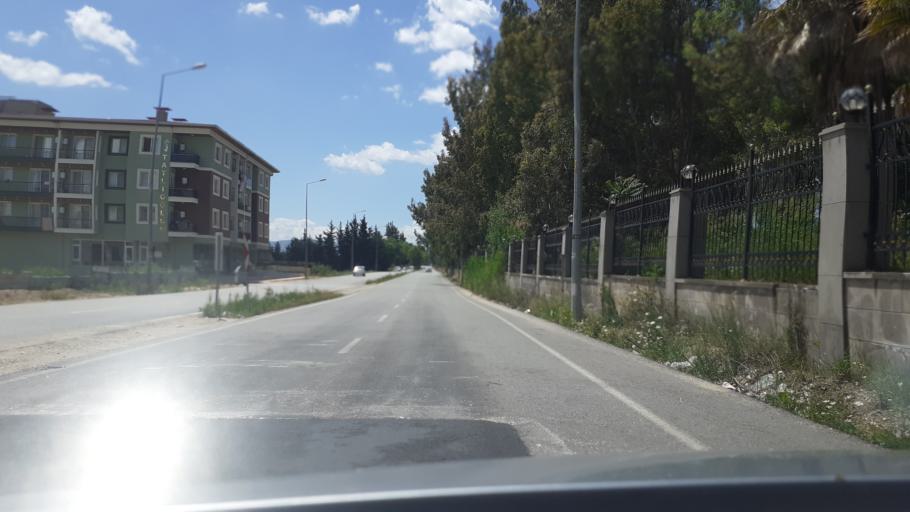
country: TR
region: Hatay
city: Anayazi
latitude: 36.3259
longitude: 36.1985
